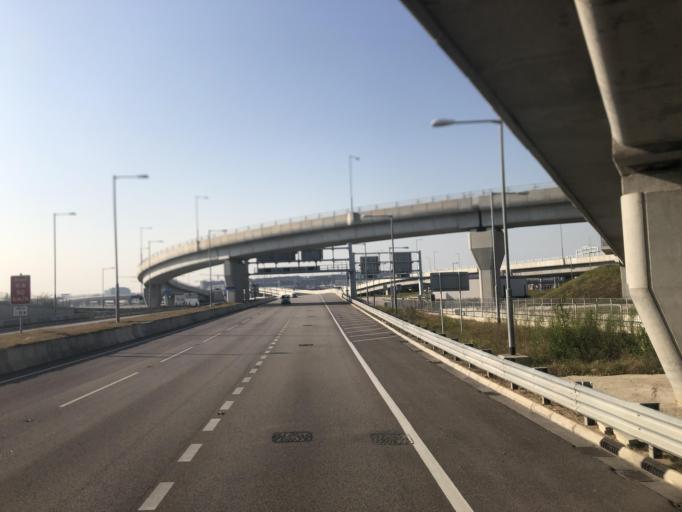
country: HK
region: Tuen Mun
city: Tuen Mun
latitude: 22.3125
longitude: 113.9532
